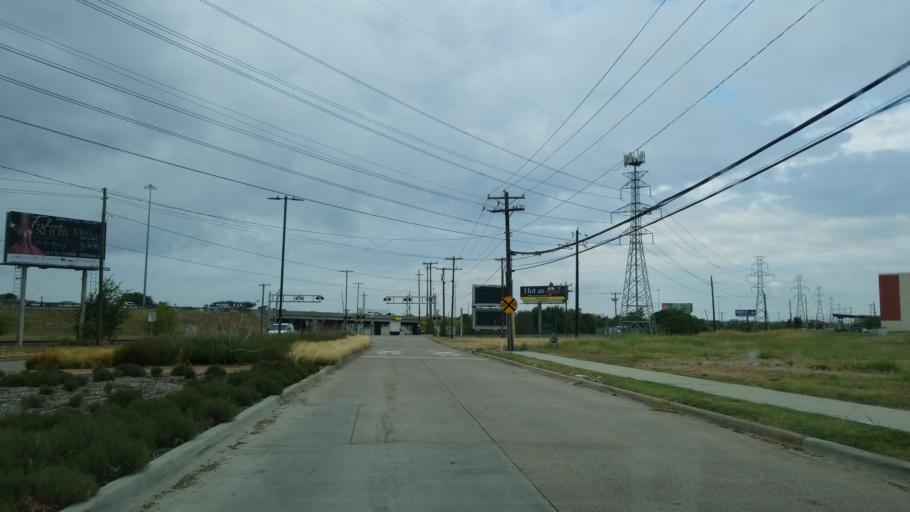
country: US
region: Texas
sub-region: Dallas County
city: Garland
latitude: 32.8788
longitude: -96.6854
